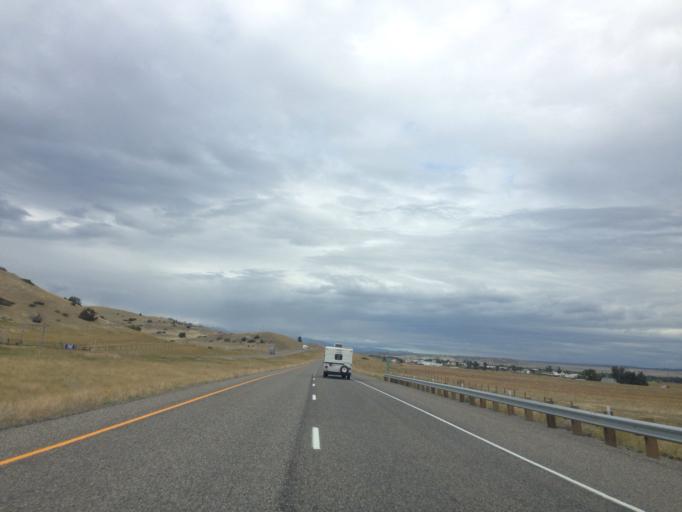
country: US
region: Montana
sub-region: Sweet Grass County
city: Big Timber
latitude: 45.7451
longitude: -109.7704
